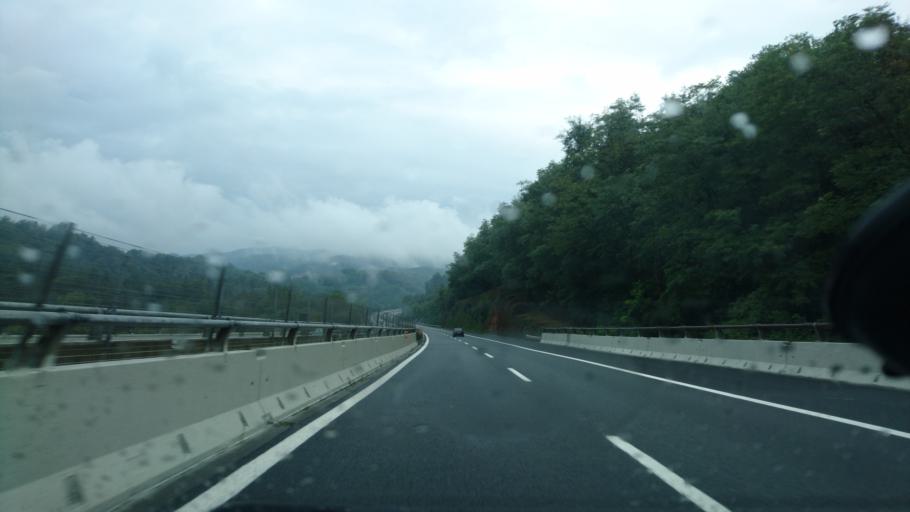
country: IT
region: Piedmont
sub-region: Provincia di Novara
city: Invorio
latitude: 45.7584
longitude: 8.5012
